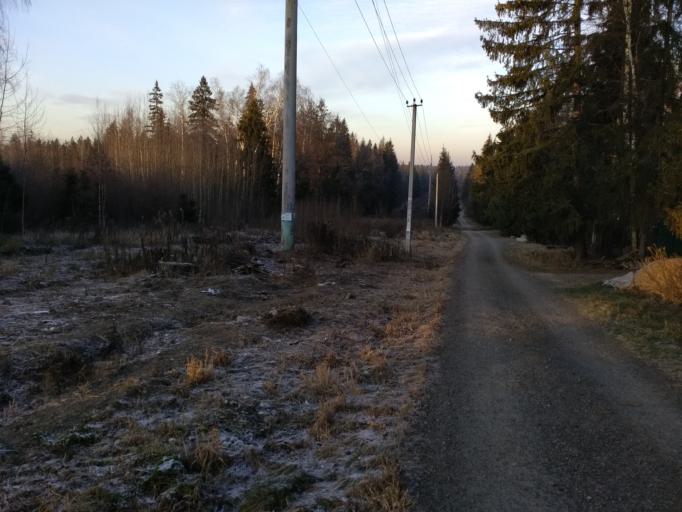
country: RU
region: Moskovskaya
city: Lugovaya
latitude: 56.0575
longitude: 37.4738
